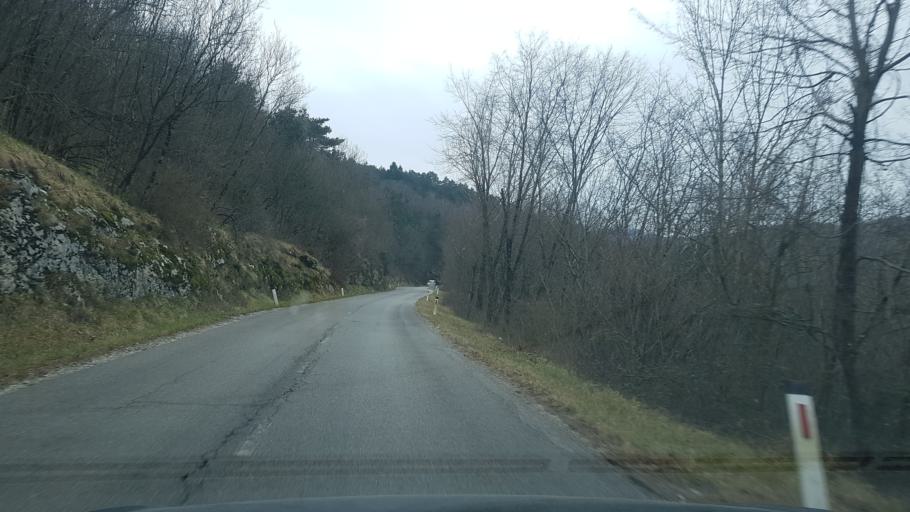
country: SI
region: Kanal
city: Kanal
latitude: 46.0385
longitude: 13.6719
